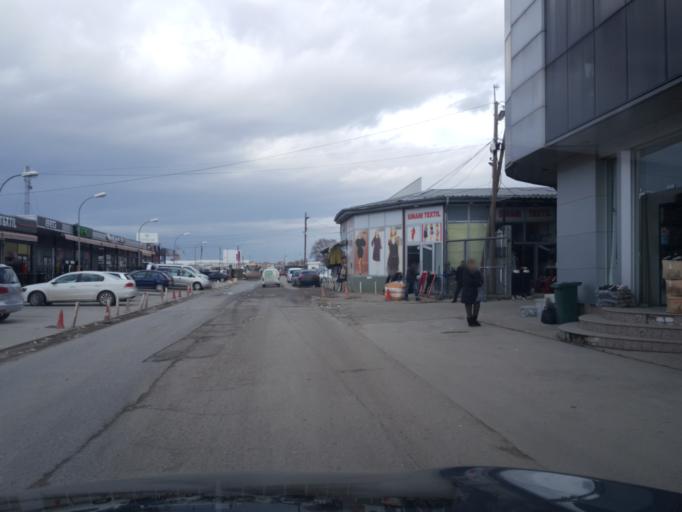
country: XK
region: Pristina
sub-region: Kosovo Polje
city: Kosovo Polje
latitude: 42.6437
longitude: 21.1286
